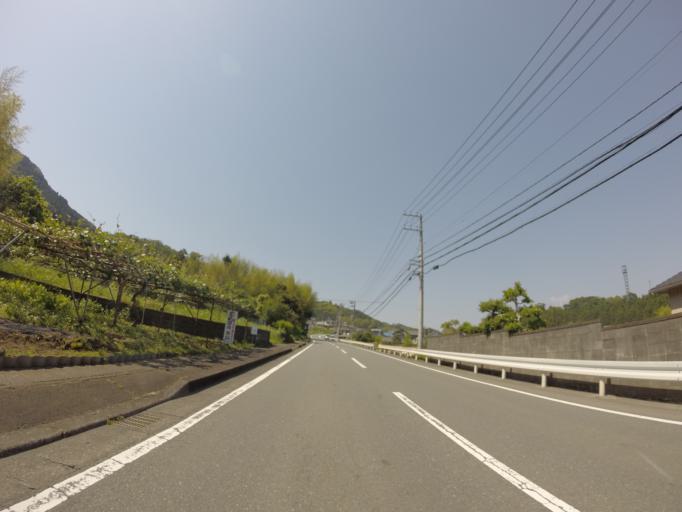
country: JP
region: Shizuoka
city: Fujinomiya
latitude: 35.2072
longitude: 138.5870
